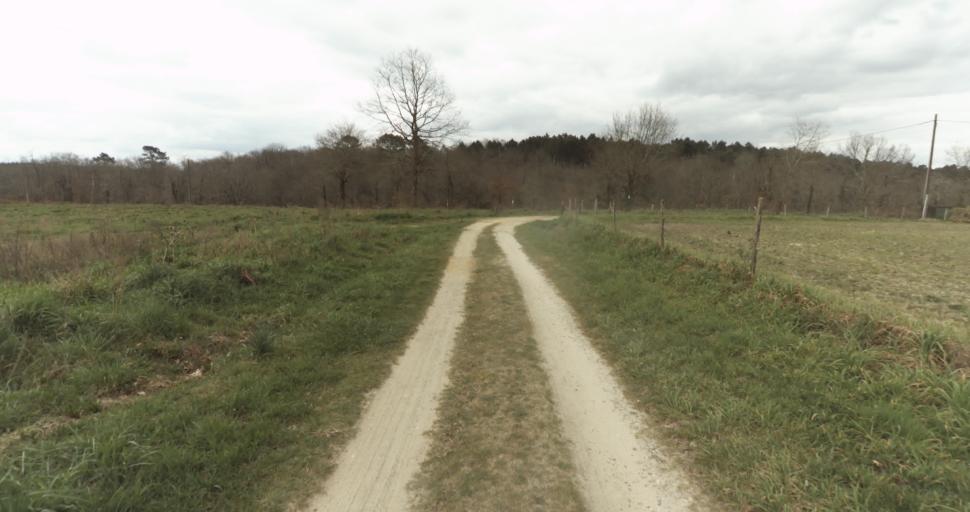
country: FR
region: Aquitaine
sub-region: Departement des Landes
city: Sarbazan
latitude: 44.0253
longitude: -0.3085
